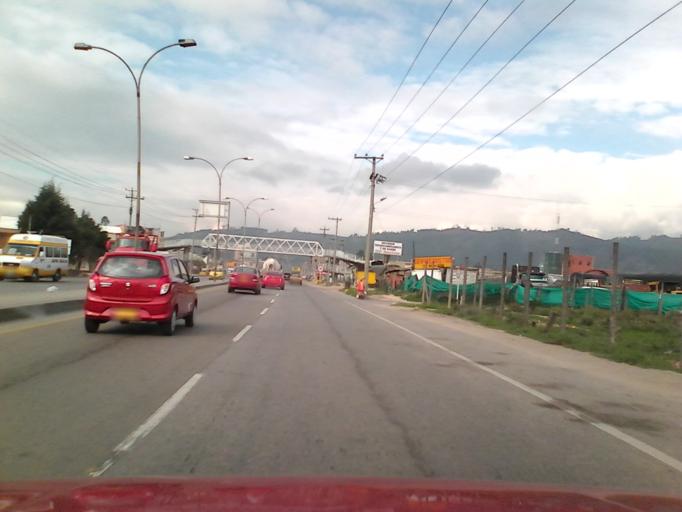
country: CO
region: Boyaca
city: Duitama
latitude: 5.8097
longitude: -73.0167
